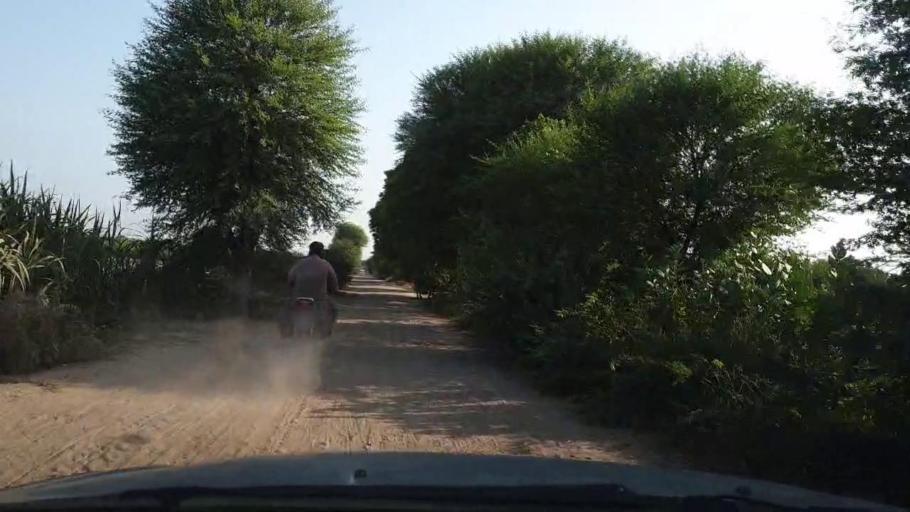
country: PK
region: Sindh
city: Tando Ghulam Ali
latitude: 25.1234
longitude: 68.9408
